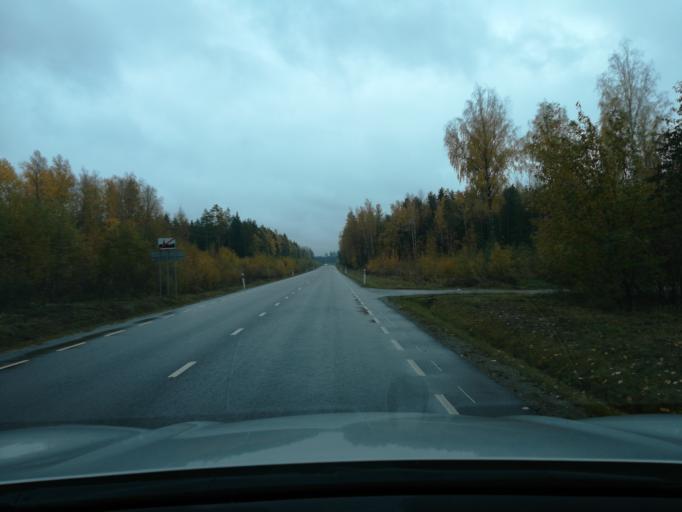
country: EE
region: Ida-Virumaa
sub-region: Johvi vald
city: Johvi
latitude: 59.3065
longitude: 27.4611
